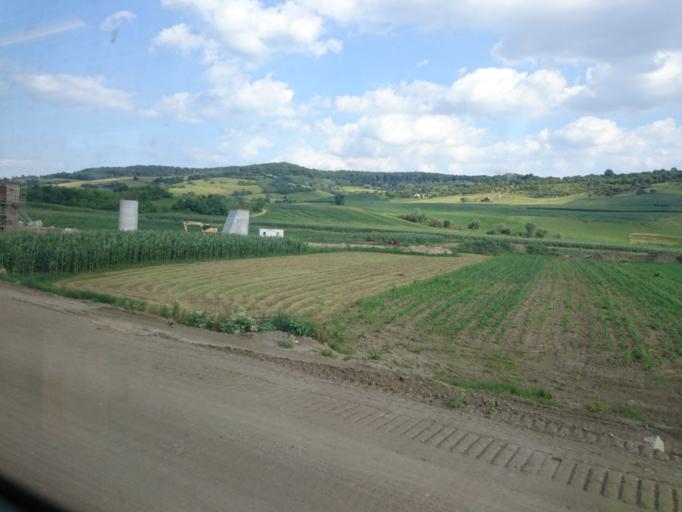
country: RO
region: Sibiu
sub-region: Oras Dumbraveni
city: Dumbraveni
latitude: 46.2144
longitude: 24.5504
